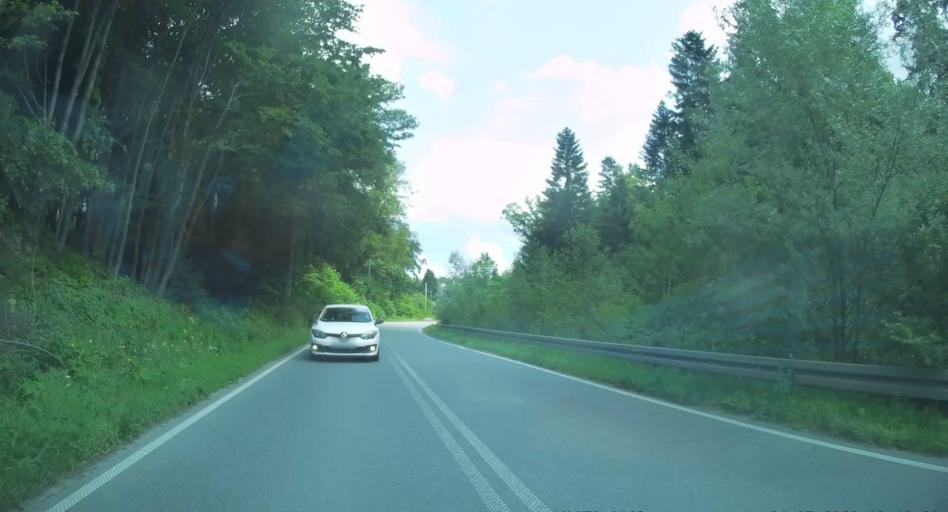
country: PL
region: Lesser Poland Voivodeship
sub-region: Powiat nowosadecki
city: Nowy Sacz
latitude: 49.6637
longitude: 20.7344
